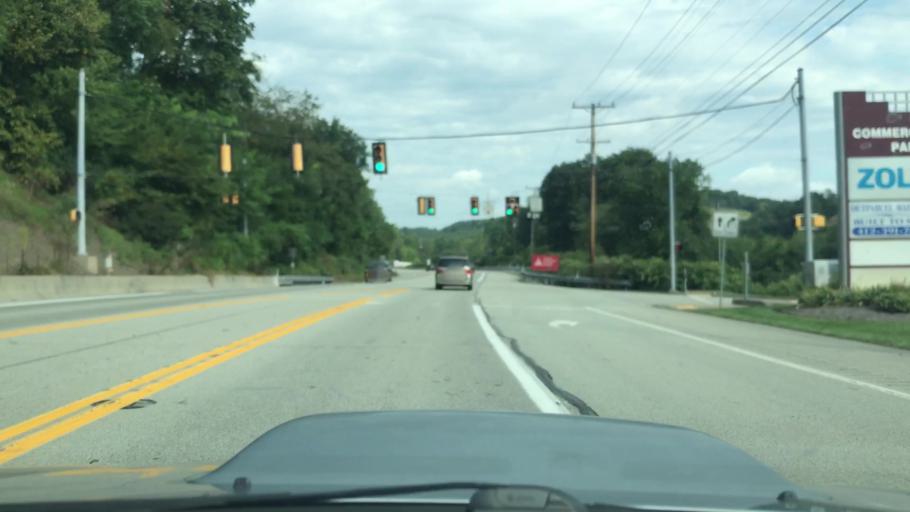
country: US
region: Pennsylvania
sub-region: Allegheny County
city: Oakmont
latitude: 40.5560
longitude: -79.8505
